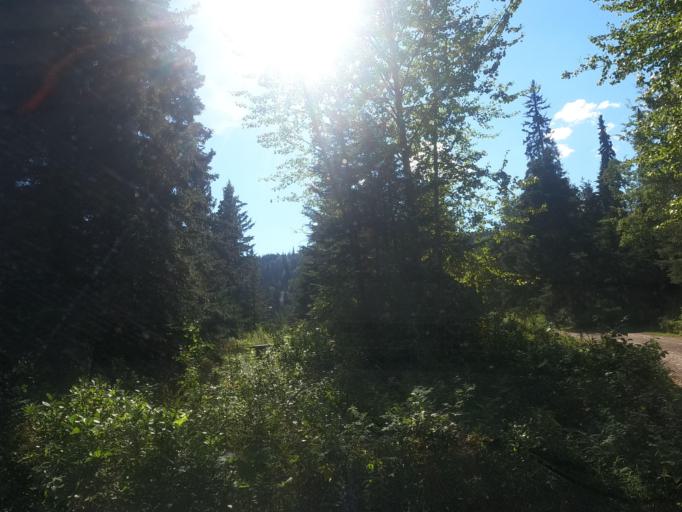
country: CA
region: British Columbia
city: Houston
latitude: 54.2861
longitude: -126.8566
